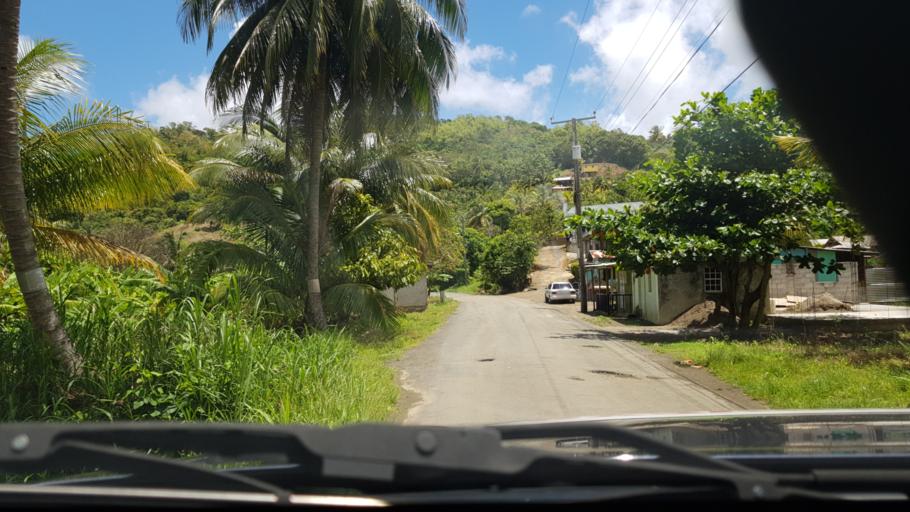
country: LC
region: Anse-la-Raye
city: Anse La Raye
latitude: 13.9461
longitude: -60.9898
